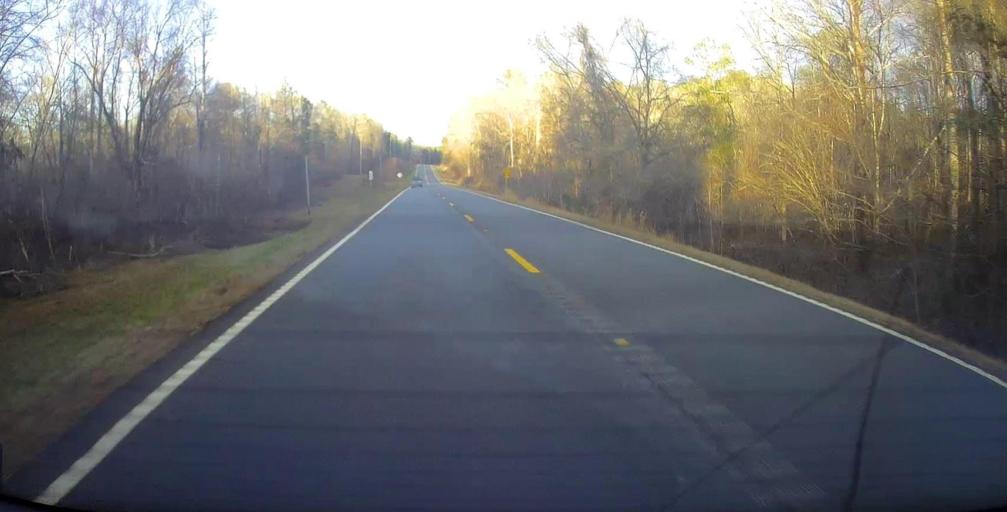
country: US
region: Georgia
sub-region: Talbot County
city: Sardis
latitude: 32.7384
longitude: -84.6094
